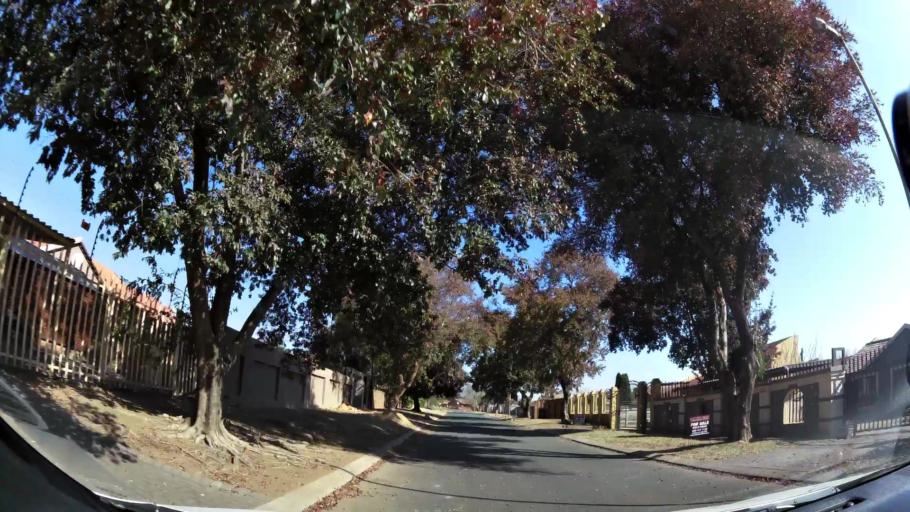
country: ZA
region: Gauteng
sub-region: City of Johannesburg Metropolitan Municipality
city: Johannesburg
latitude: -26.2394
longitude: 28.1032
